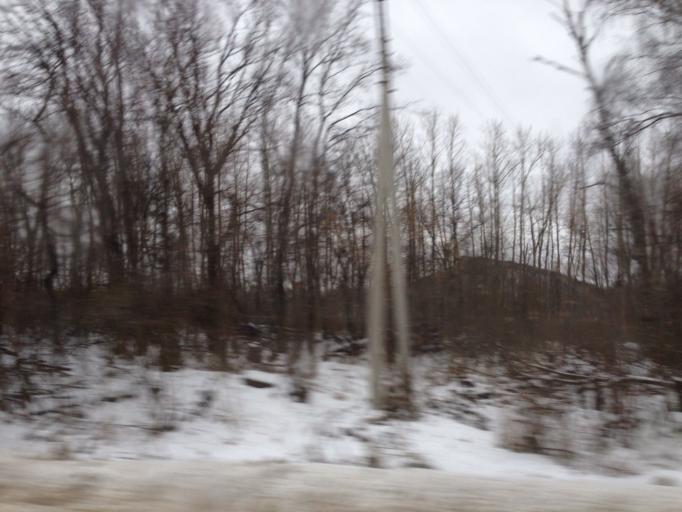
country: RU
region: Tula
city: Partizan
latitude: 54.0064
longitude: 38.1082
